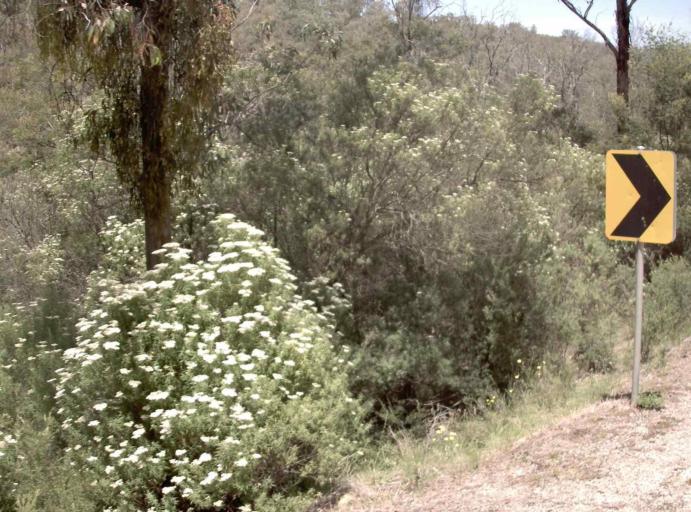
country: AU
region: Victoria
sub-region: East Gippsland
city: Bairnsdale
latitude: -37.4586
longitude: 147.8334
